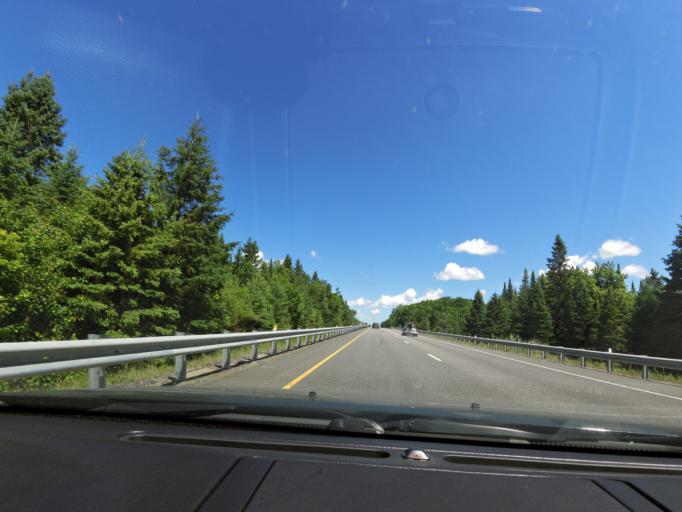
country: CA
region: Ontario
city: Bracebridge
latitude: 45.1445
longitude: -79.3111
